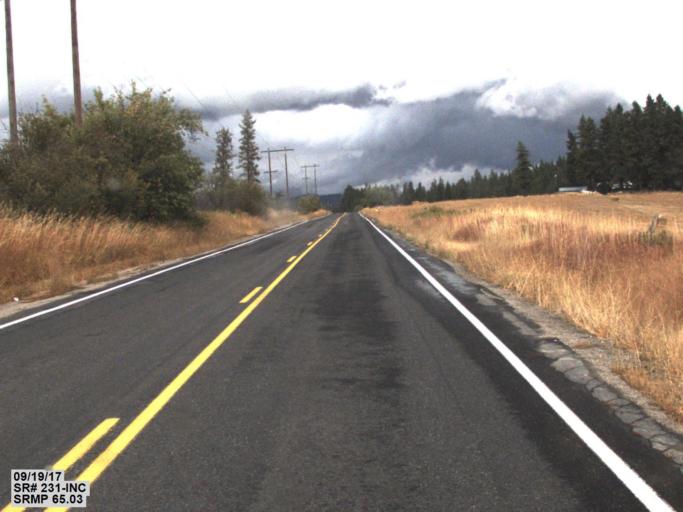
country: US
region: Washington
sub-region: Stevens County
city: Chewelah
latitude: 48.0859
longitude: -117.7579
